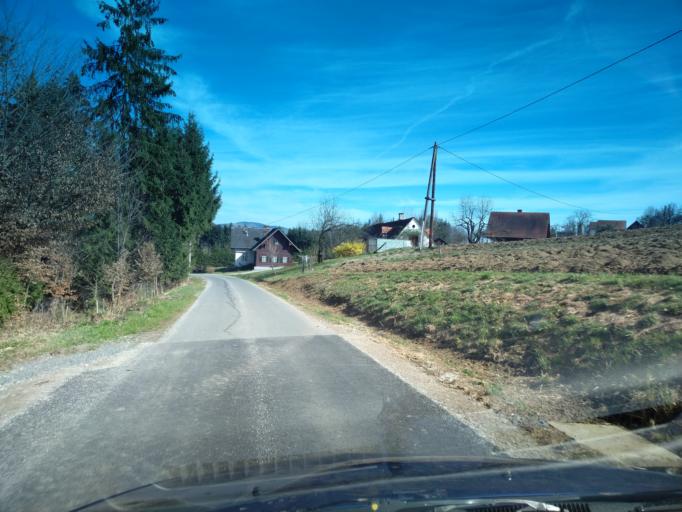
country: AT
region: Styria
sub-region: Politischer Bezirk Deutschlandsberg
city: Unterbergla
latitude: 46.7949
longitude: 15.3115
